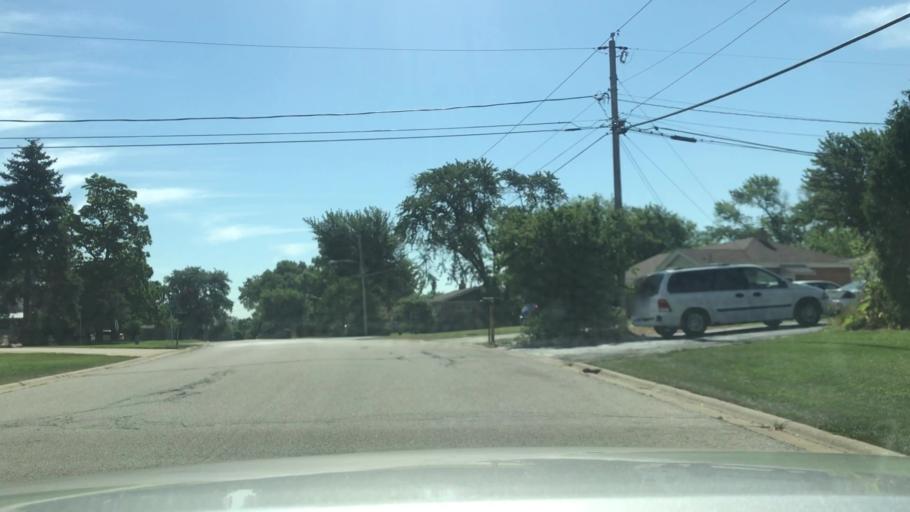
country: US
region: Illinois
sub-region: Cook County
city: Hickory Hills
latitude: 41.7366
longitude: -87.8282
